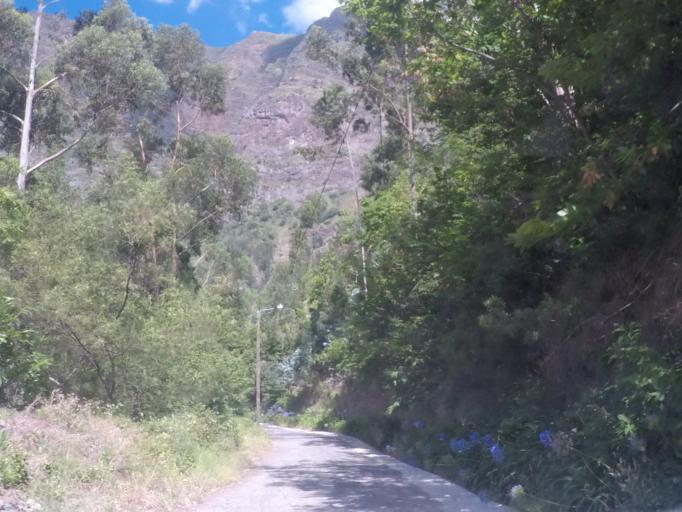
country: PT
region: Madeira
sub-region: Camara de Lobos
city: Curral das Freiras
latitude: 32.7149
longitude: -16.9751
